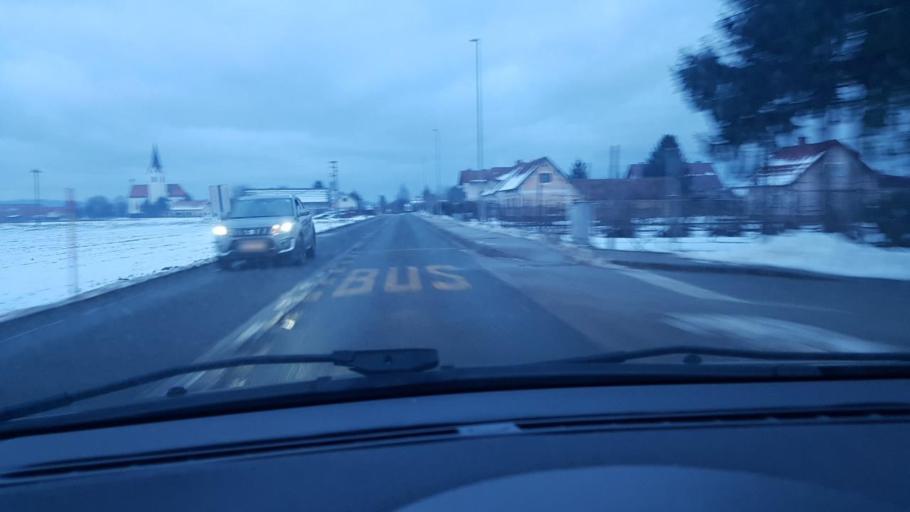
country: SI
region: Hajdina
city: Spodnja Hajdina
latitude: 46.4032
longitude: 15.8343
